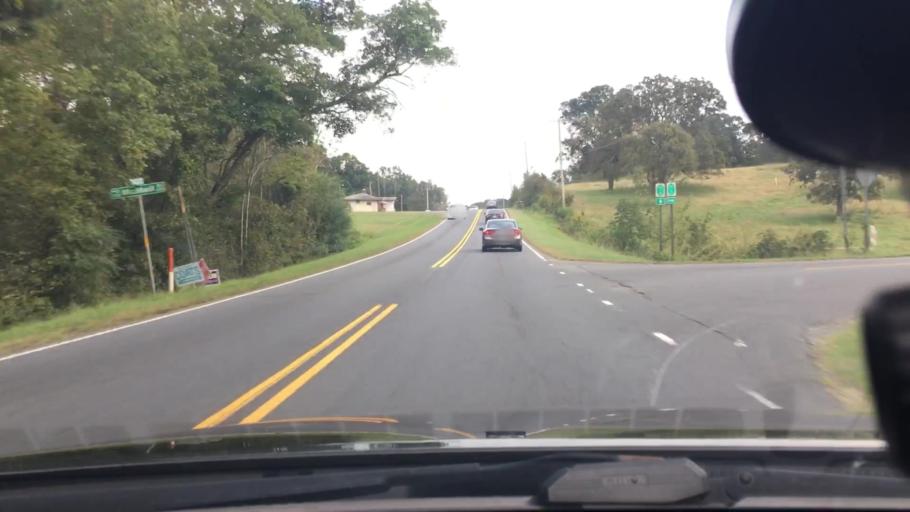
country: US
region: North Carolina
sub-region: Stanly County
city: Albemarle
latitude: 35.3215
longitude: -80.1243
